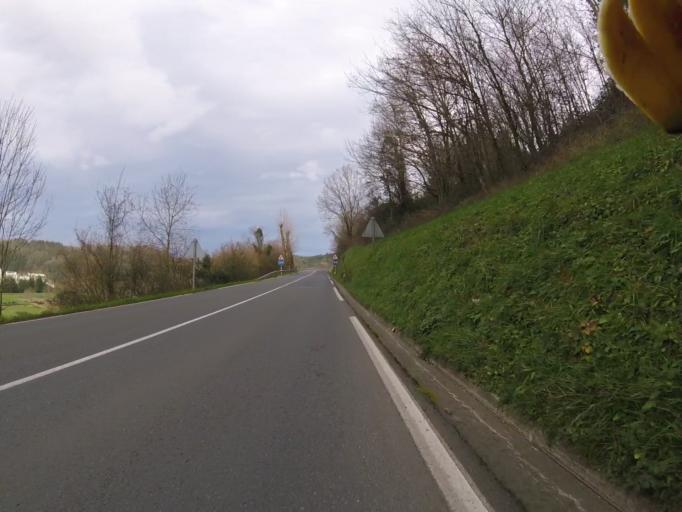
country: ES
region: Basque Country
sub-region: Provincia de Guipuzcoa
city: Cestona
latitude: 43.2562
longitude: -2.2569
